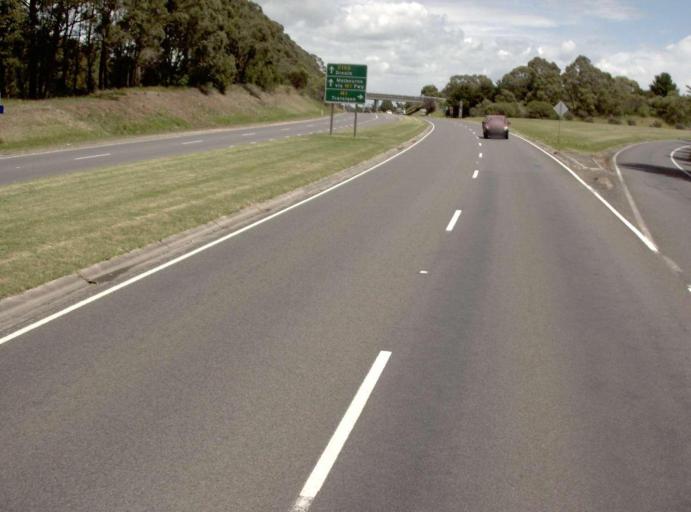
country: AU
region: Victoria
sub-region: Baw Baw
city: Warragul
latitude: -38.1422
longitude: 145.8886
